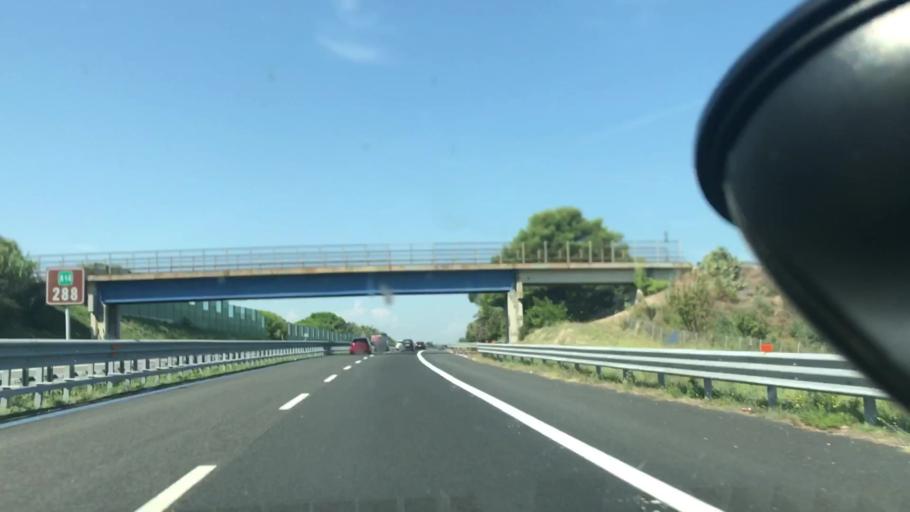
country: IT
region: Molise
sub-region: Provincia di Campobasso
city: Petacciato
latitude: 42.0165
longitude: 14.9082
